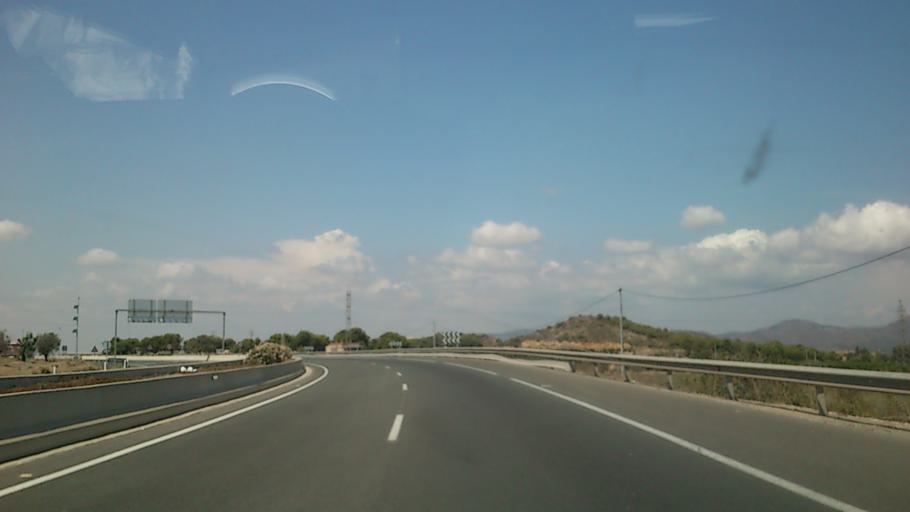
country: ES
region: Valencia
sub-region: Provincia de Valencia
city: Museros
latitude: 39.5924
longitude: -0.3601
